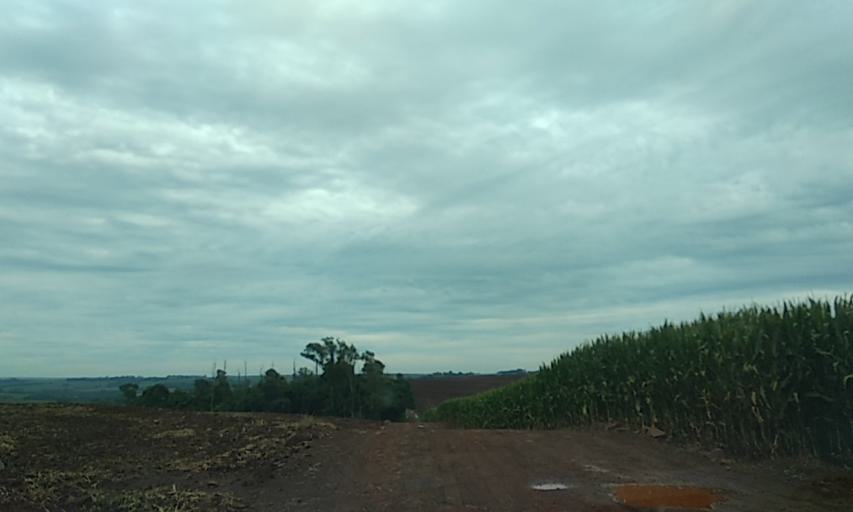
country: BR
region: Parana
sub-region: Marechal Candido Rondon
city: Marechal Candido Rondon
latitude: -24.5324
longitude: -54.0885
